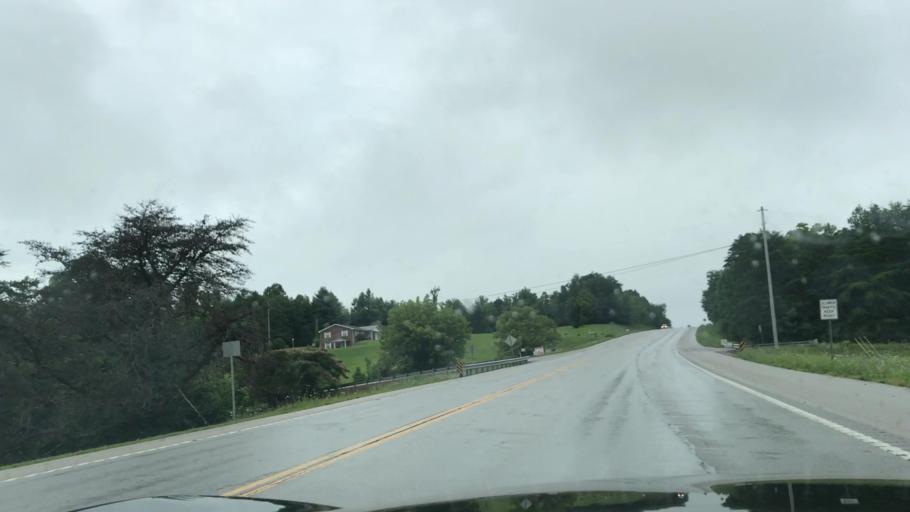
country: US
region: Tennessee
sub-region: Scott County
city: Huntsville
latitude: 36.3616
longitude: -84.5832
